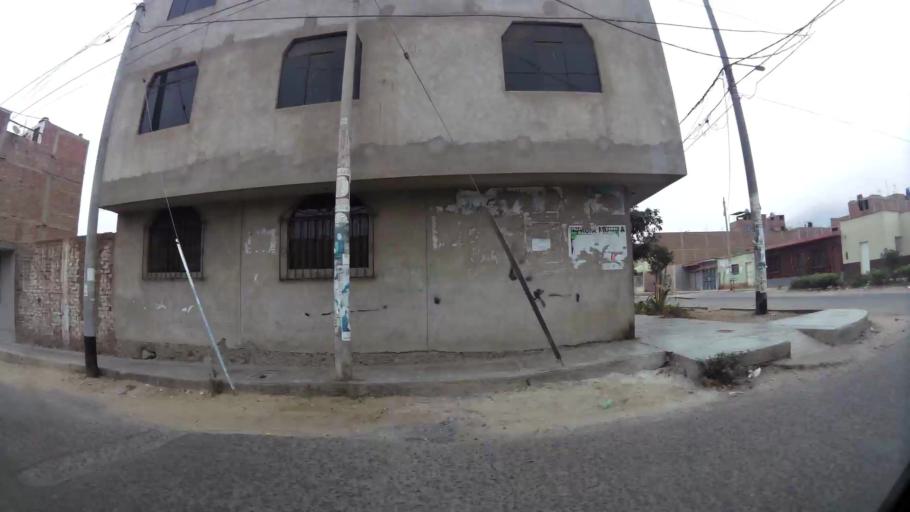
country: PE
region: La Libertad
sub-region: Provincia de Trujillo
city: La Esperanza
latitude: -8.0806
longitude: -79.0482
